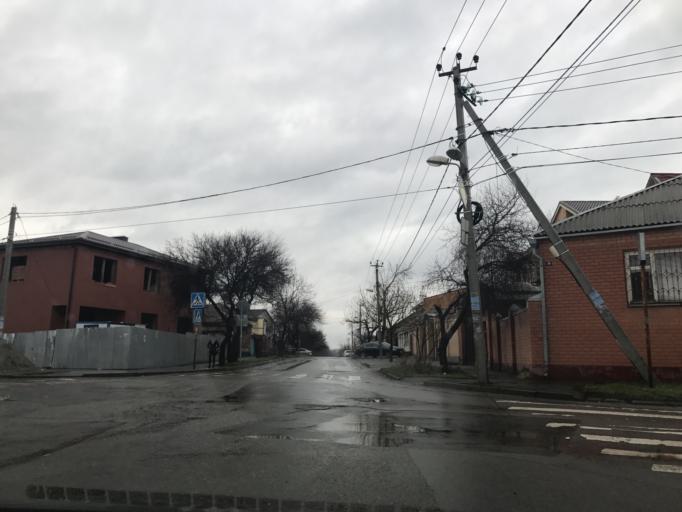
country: RU
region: Rostov
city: Rostov-na-Donu
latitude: 47.2338
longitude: 39.6772
